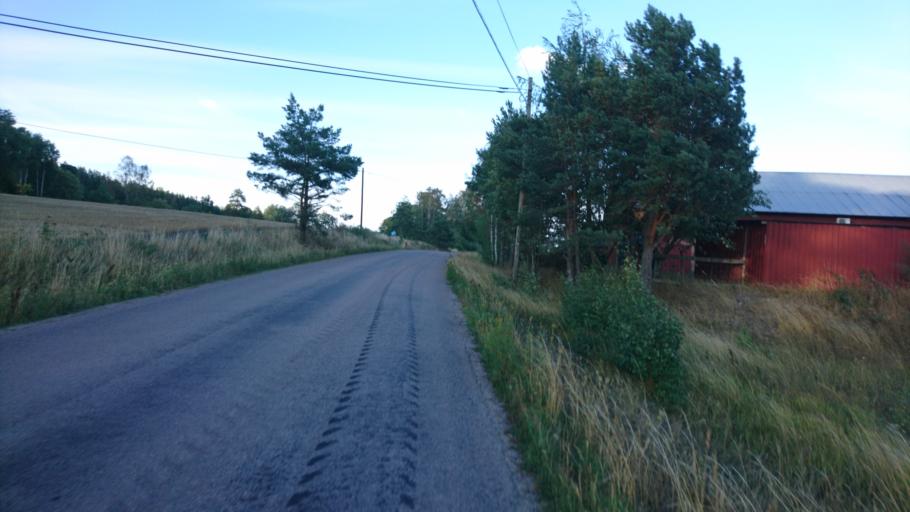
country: SE
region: Soedermanland
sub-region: Strangnas Kommun
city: Stallarholmen
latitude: 59.3995
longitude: 17.2661
